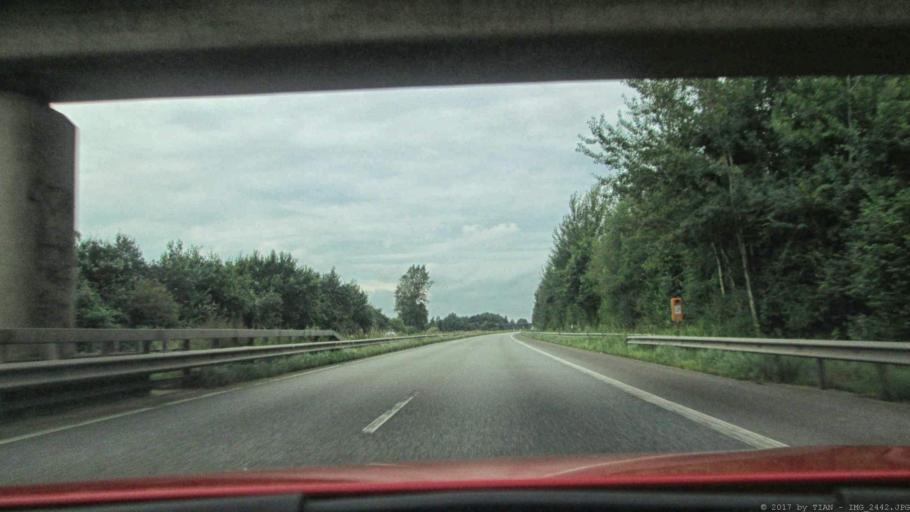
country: DE
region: Schleswig-Holstein
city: Bornsen
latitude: 53.4610
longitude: 10.2879
